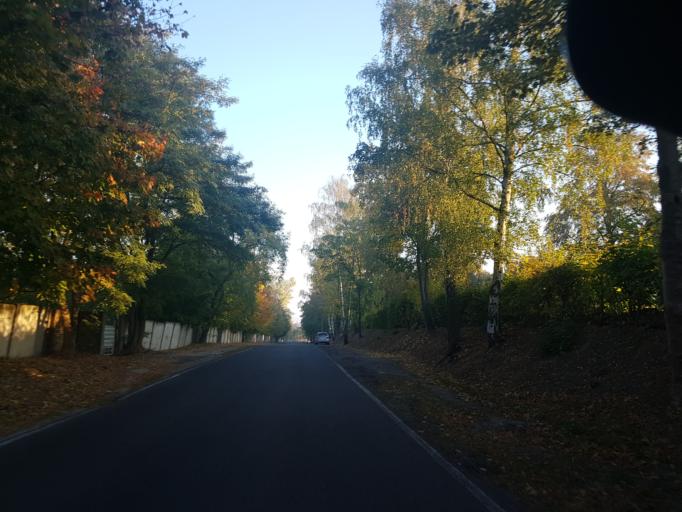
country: DE
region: Brandenburg
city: Juterbog
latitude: 51.9818
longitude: 13.0720
